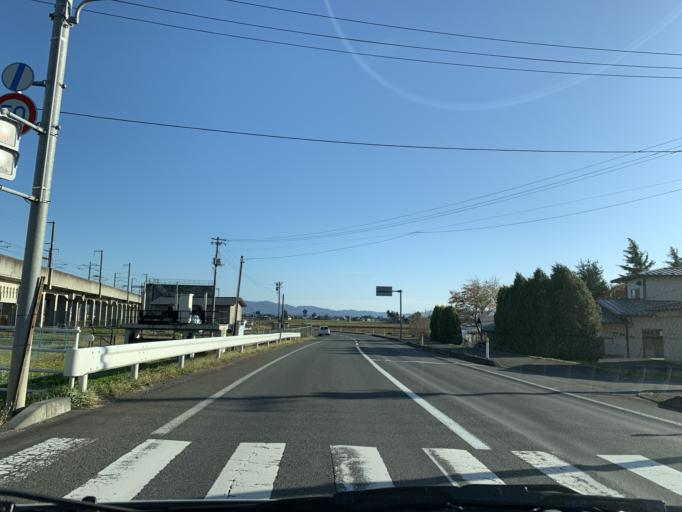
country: JP
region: Iwate
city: Kitakami
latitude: 39.2184
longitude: 141.1338
